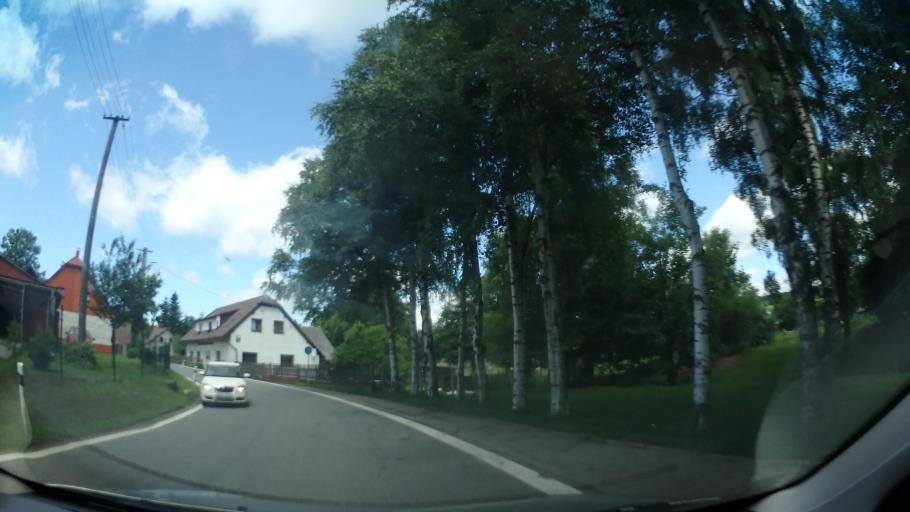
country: CZ
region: Vysocina
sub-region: Okres Zd'ar nad Sazavou
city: Nove Mesto na Morave
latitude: 49.6303
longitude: 16.0445
